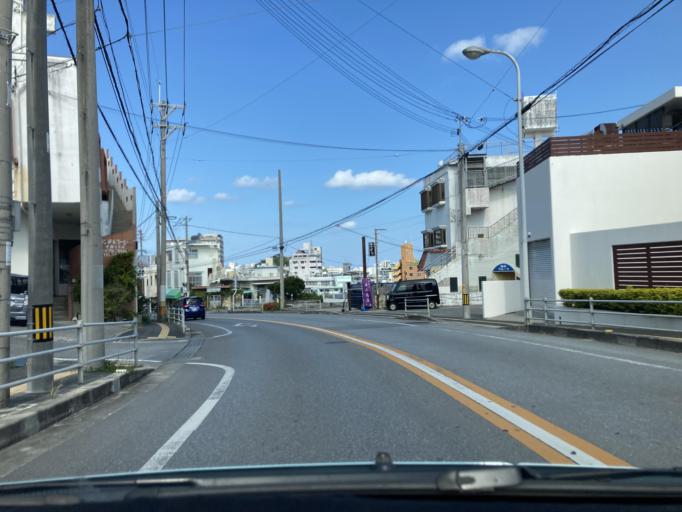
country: JP
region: Okinawa
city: Tomigusuku
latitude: 26.1896
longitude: 127.6807
